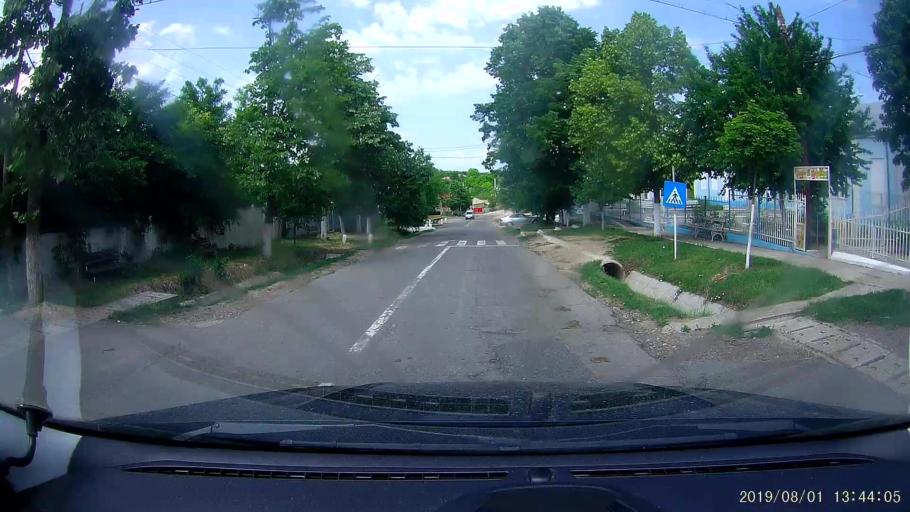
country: RO
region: Galati
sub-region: Comuna Oancea
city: Oancea
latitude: 45.9189
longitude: 28.1130
